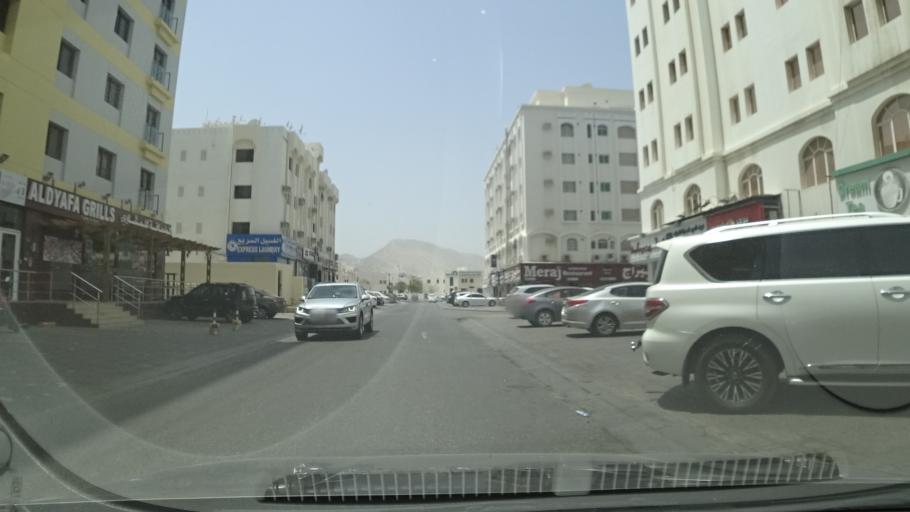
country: OM
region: Muhafazat Masqat
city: Bawshar
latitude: 23.5943
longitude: 58.4241
